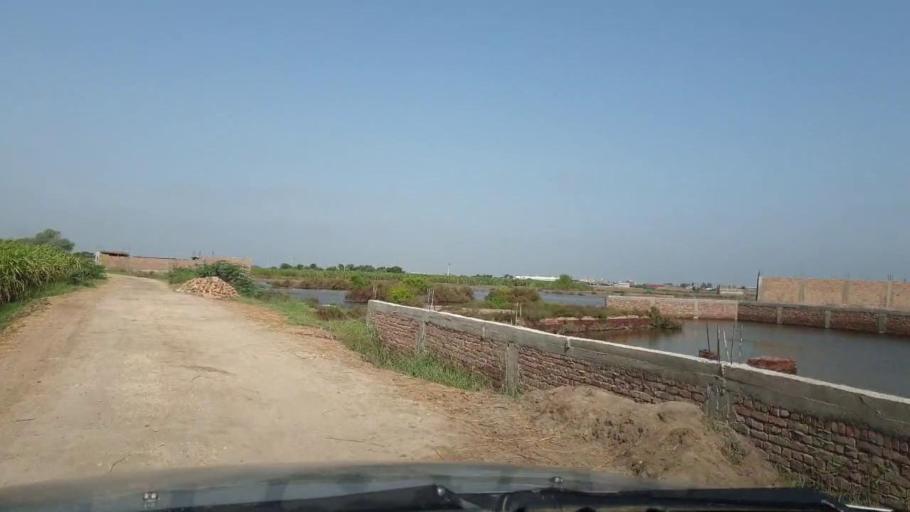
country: PK
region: Sindh
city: Matli
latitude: 25.0512
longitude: 68.6428
